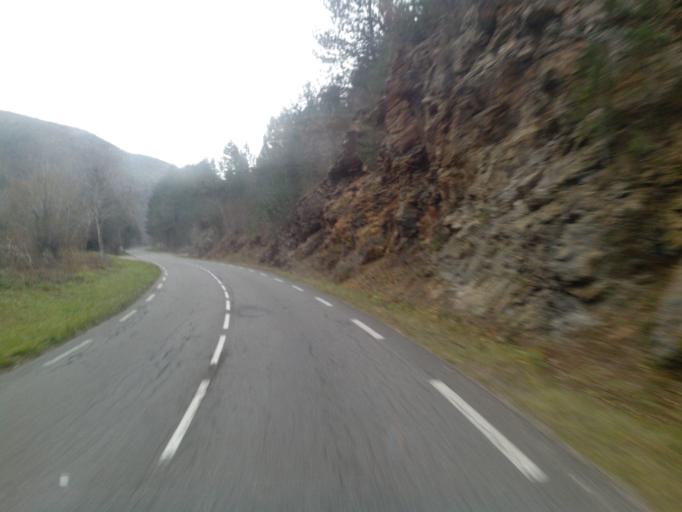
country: FR
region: Languedoc-Roussillon
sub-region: Departement de la Lozere
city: Florac
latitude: 44.3033
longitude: 3.5968
